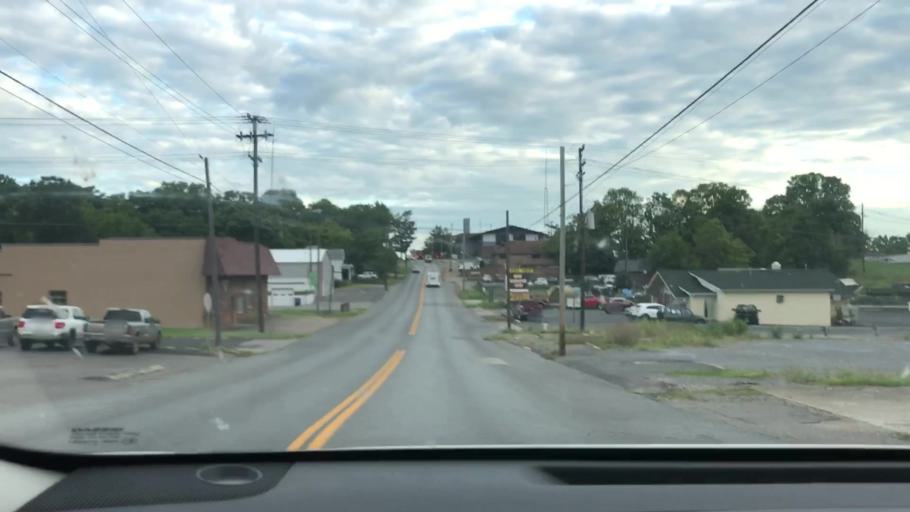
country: US
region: Kentucky
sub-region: Calloway County
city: Murray
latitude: 36.6055
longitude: -88.3022
